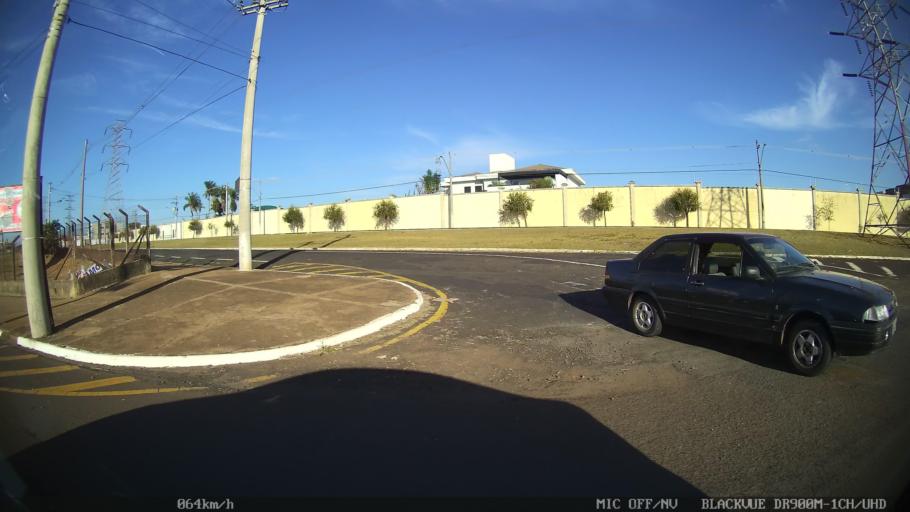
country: BR
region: Sao Paulo
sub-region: Franca
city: Franca
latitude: -20.5125
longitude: -47.3761
